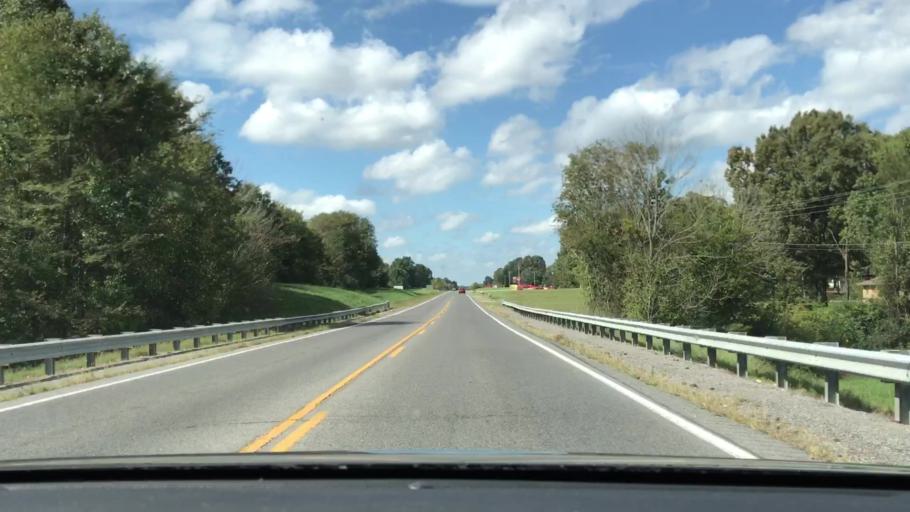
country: US
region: Kentucky
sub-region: Livingston County
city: Ledbetter
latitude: 37.0068
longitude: -88.4588
